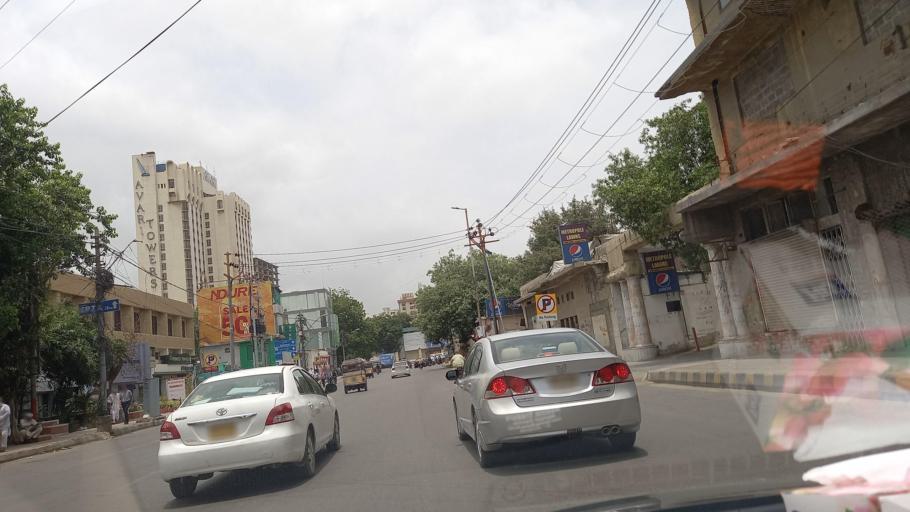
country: PK
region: Sindh
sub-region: Karachi District
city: Karachi
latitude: 24.8510
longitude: 67.0305
